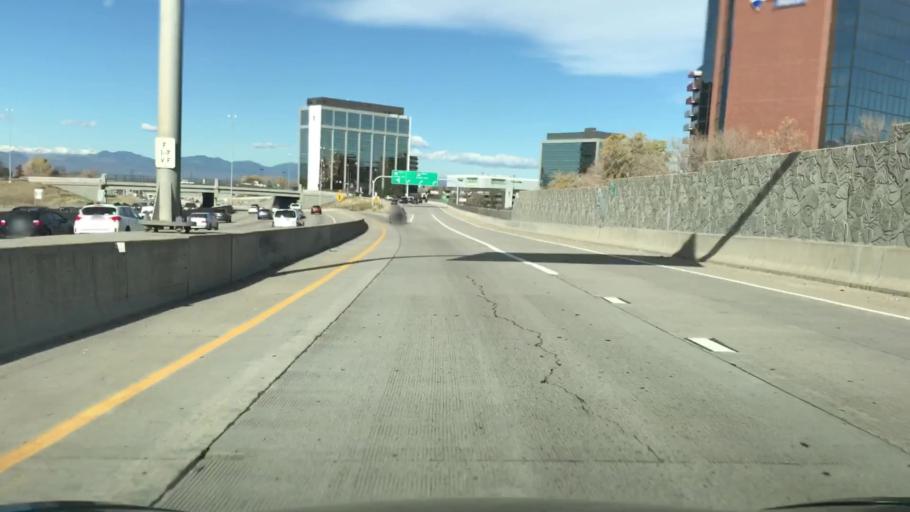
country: US
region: Colorado
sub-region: Arapahoe County
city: Glendale
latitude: 39.6819
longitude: -104.9372
